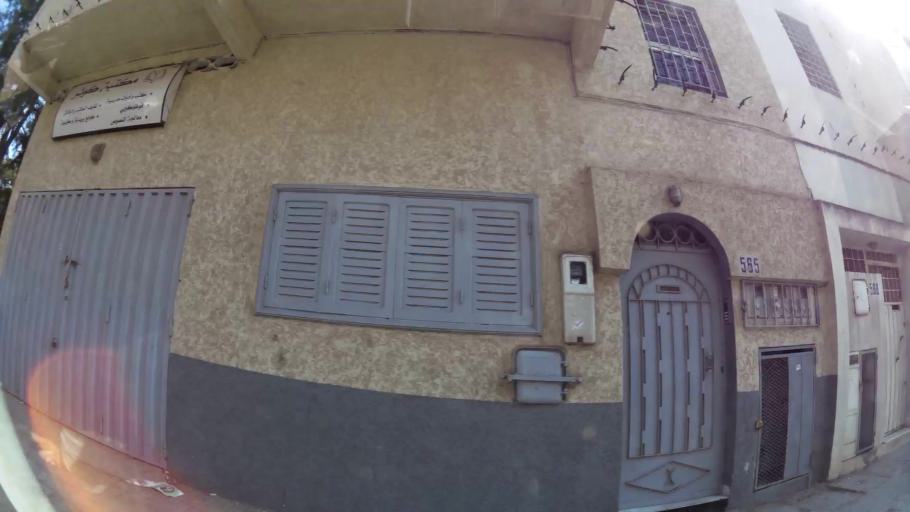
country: MA
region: Rabat-Sale-Zemmour-Zaer
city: Sale
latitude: 34.0421
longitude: -6.7787
